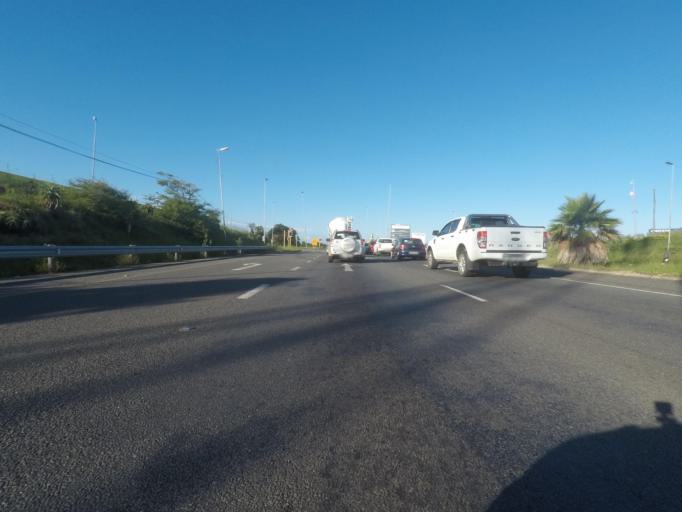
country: ZA
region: Eastern Cape
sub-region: Buffalo City Metropolitan Municipality
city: East London
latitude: -33.0389
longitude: 27.8320
